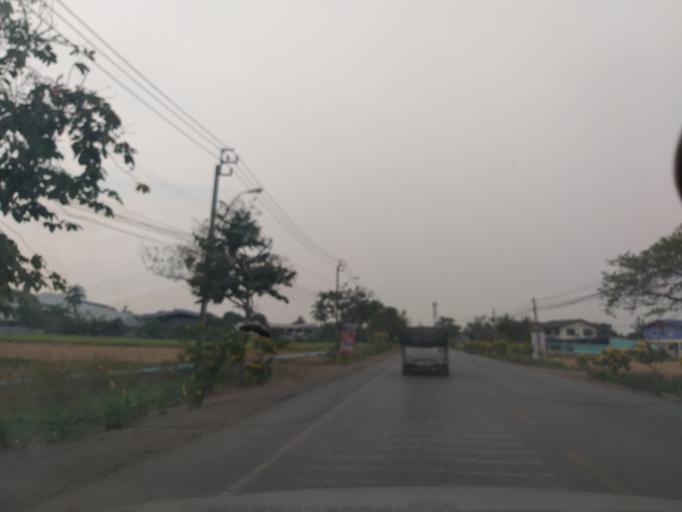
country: TH
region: Bangkok
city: Nong Chok
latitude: 13.8304
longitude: 100.9133
